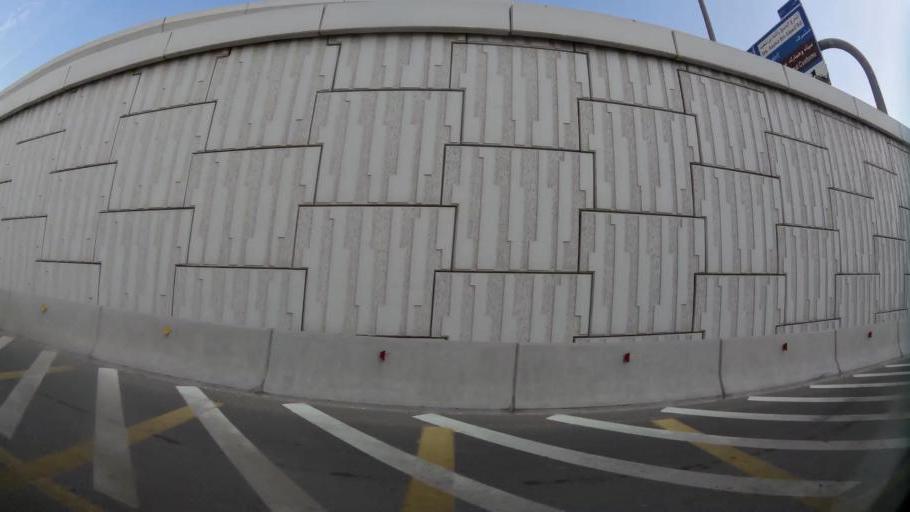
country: AE
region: Ajman
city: Ajman
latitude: 25.3907
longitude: 55.4720
